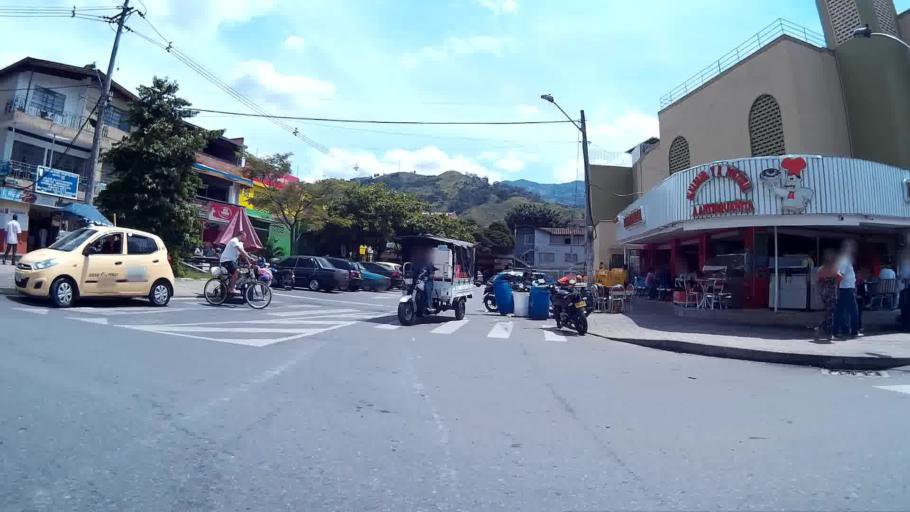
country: CO
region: Antioquia
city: Medellin
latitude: 6.2561
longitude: -75.6162
